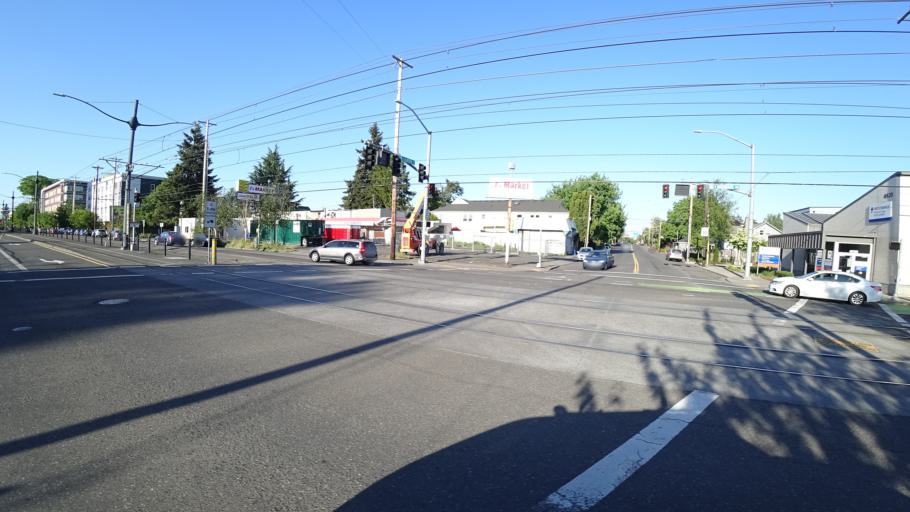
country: US
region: Oregon
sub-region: Multnomah County
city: Portland
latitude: 45.5590
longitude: -122.6824
